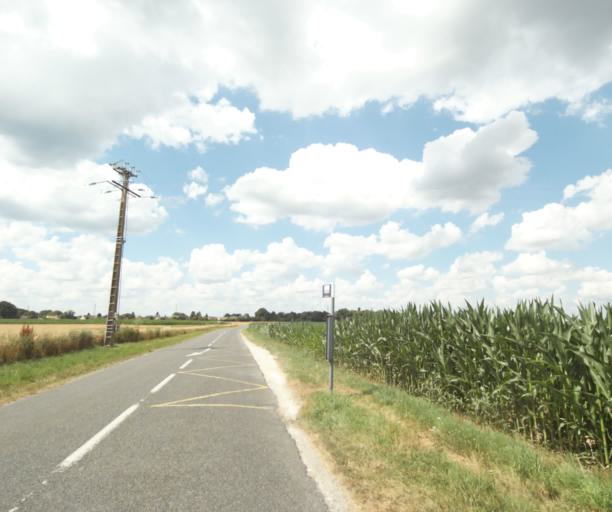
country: FR
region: Ile-de-France
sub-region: Departement de Seine-et-Marne
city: Hericy
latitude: 48.4434
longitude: 2.7854
